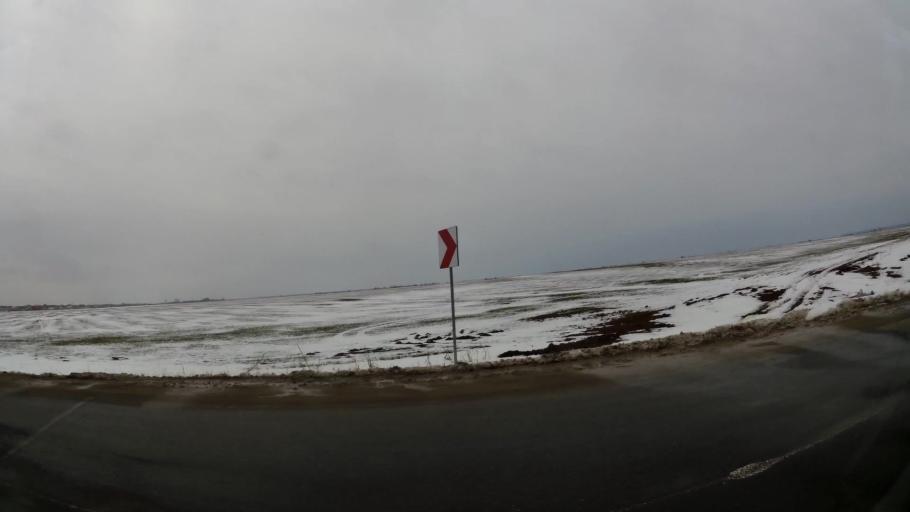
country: RO
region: Ilfov
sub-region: Comuna Tunari
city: Tunari
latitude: 44.5539
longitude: 26.1688
